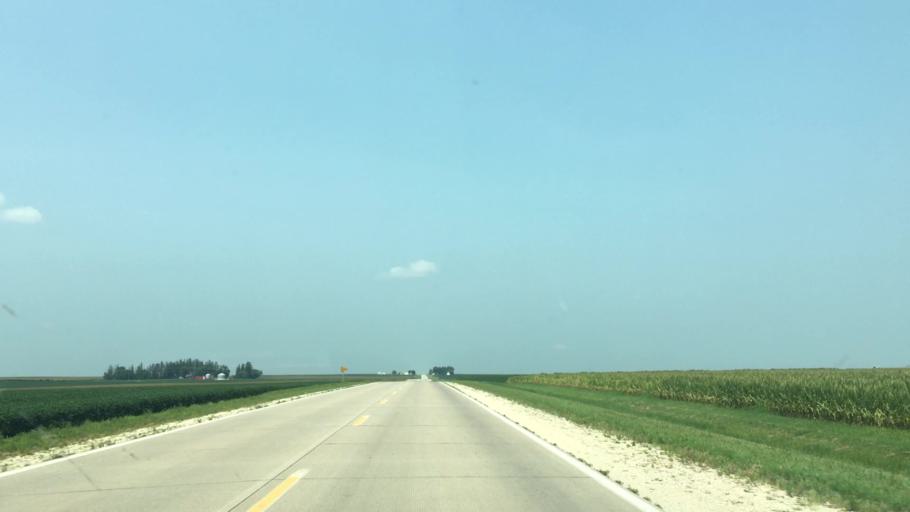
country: US
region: Iowa
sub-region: Fayette County
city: Oelwein
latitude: 42.6914
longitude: -91.8051
